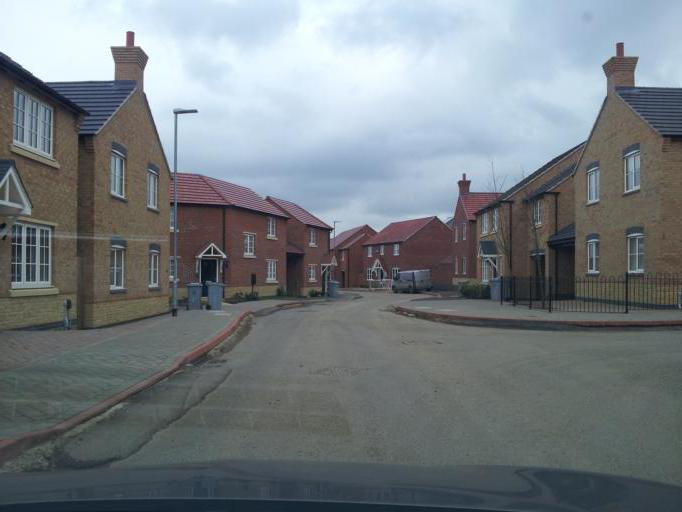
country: GB
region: England
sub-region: Lincolnshire
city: Great Gonerby
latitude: 52.9201
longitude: -0.6609
